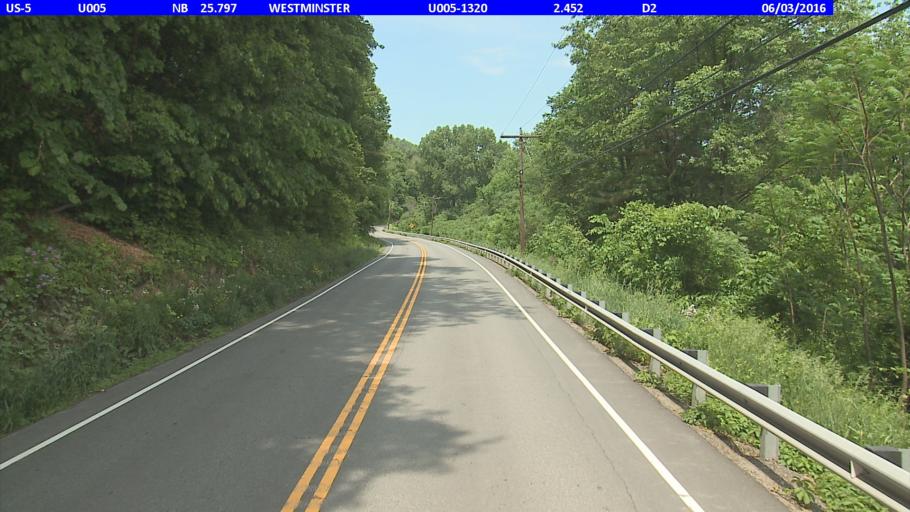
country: US
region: Vermont
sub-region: Windham County
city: Bellows Falls
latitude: 43.0543
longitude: -72.4690
